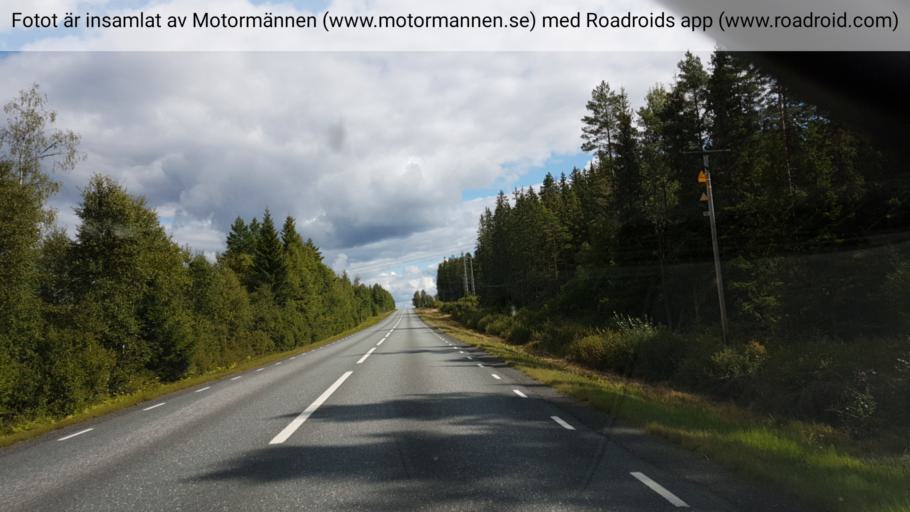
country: SE
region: Joenkoeping
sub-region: Nassjo Kommun
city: Nassjo
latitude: 57.7863
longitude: 14.6665
